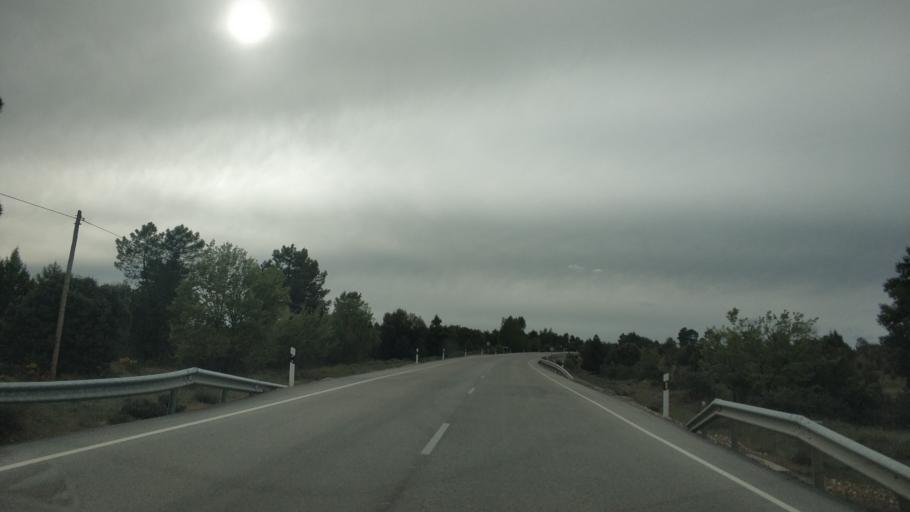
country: ES
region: Castille and Leon
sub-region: Provincia de Soria
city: Quintanas de Gormaz
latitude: 41.5235
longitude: -2.9387
